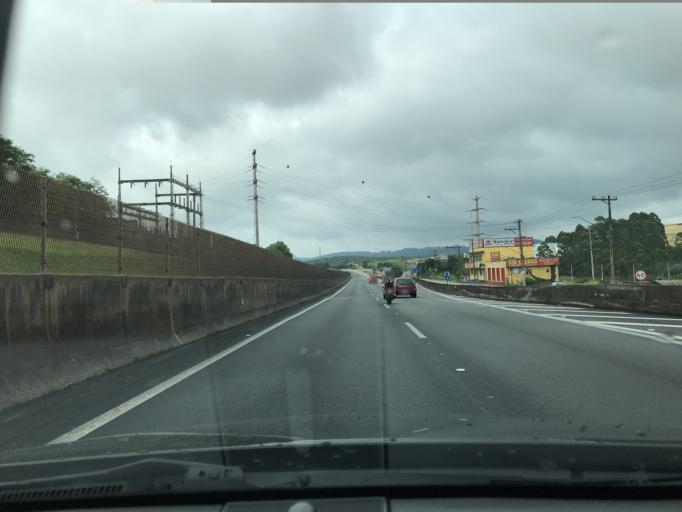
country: BR
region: Sao Paulo
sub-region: Vargem Grande Paulista
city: Vargem Grande Paulista
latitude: -23.6073
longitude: -47.0117
